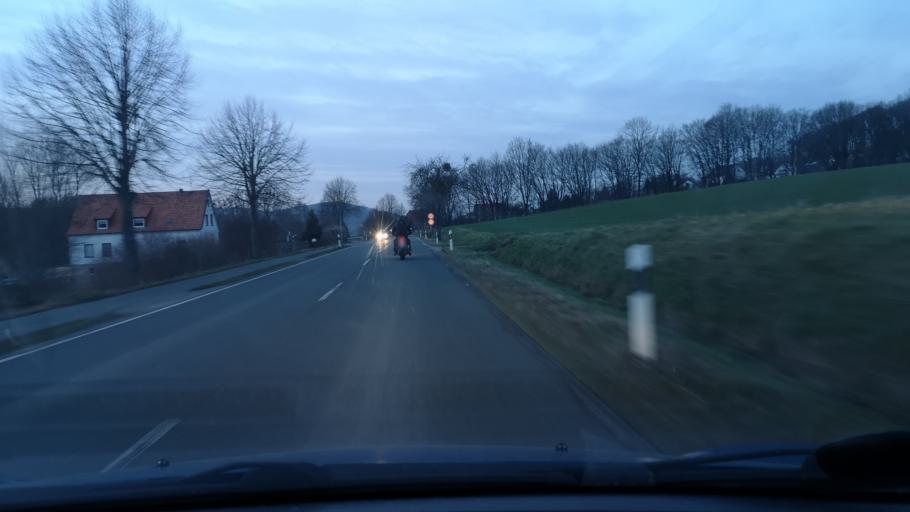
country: DE
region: Lower Saxony
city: Salzhemmendorf
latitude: 52.0587
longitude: 9.5922
